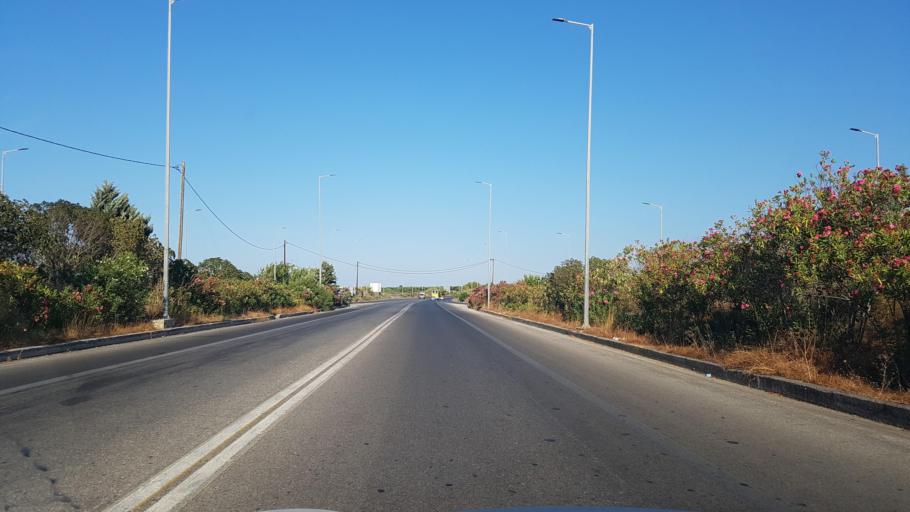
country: GR
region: Crete
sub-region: Nomos Chanias
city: Kolympari
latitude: 35.5299
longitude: 23.7844
